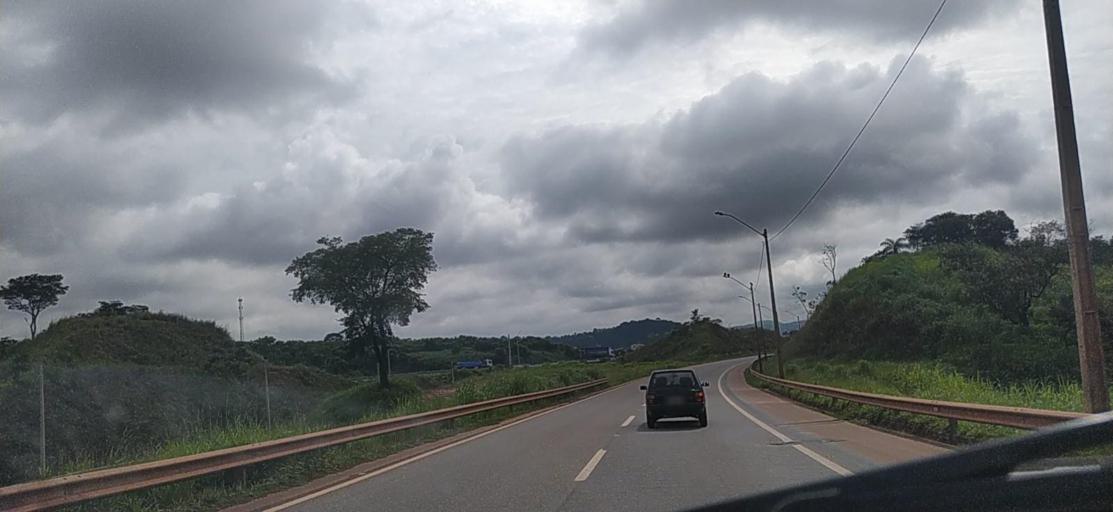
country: BR
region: Minas Gerais
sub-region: Betim
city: Betim
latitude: -19.9883
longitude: -44.2024
